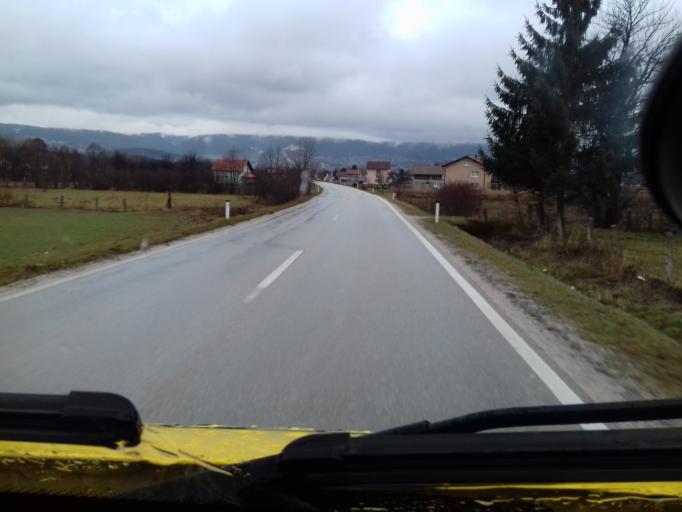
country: BA
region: Federation of Bosnia and Herzegovina
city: Bugojno
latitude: 44.0687
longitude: 17.4835
